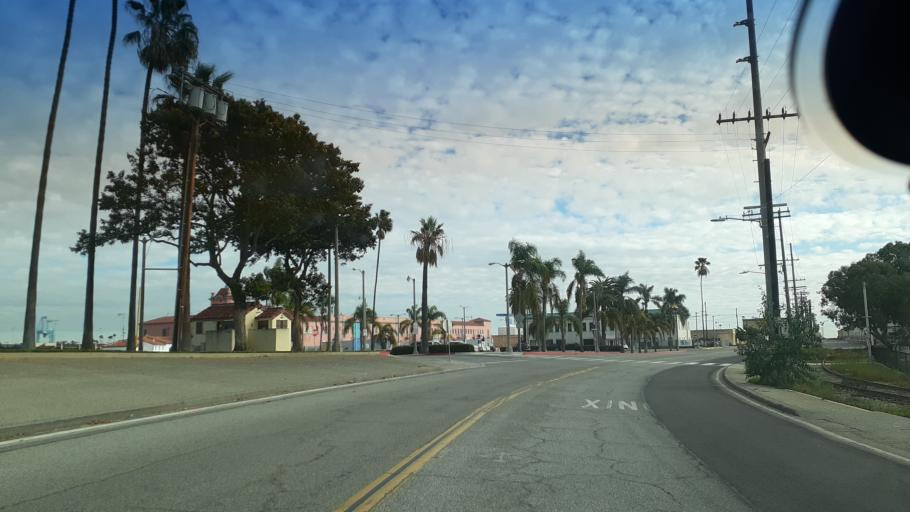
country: US
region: California
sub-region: Los Angeles County
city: San Pedro
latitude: 33.7284
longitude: -118.2756
